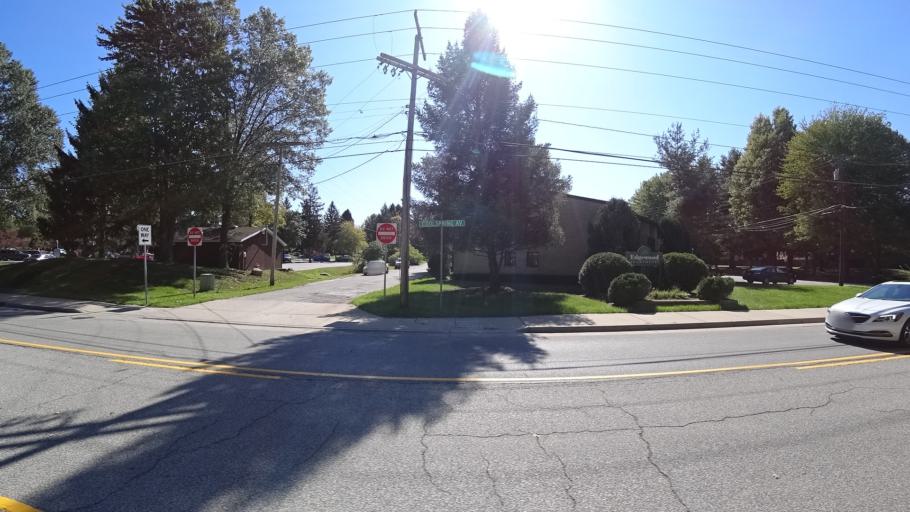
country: US
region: Indiana
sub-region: LaPorte County
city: Trail Creek
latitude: 41.6948
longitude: -86.8774
